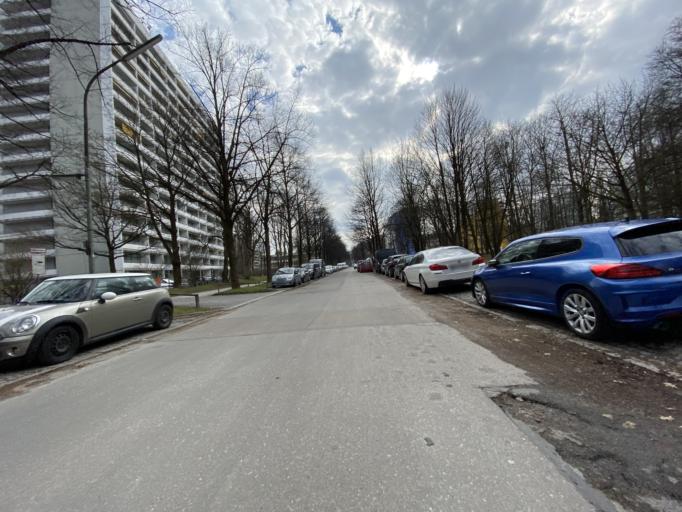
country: DE
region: Bavaria
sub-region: Upper Bavaria
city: Unterfoehring
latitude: 48.1722
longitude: 11.6436
